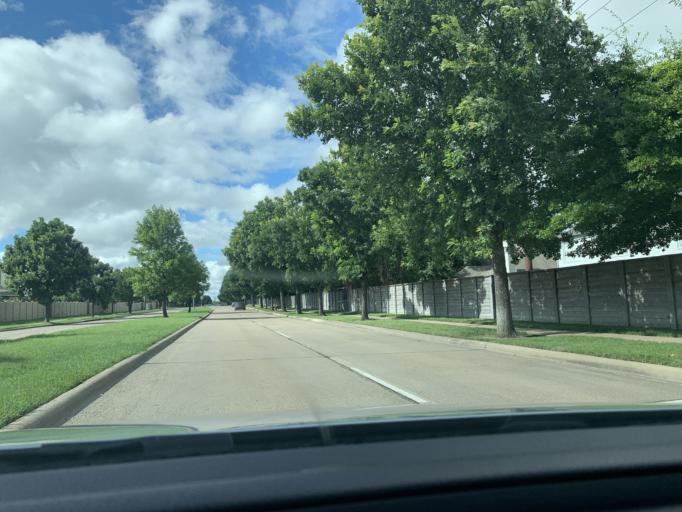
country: US
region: Texas
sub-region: Dallas County
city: Grand Prairie
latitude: 32.6607
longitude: -97.0153
